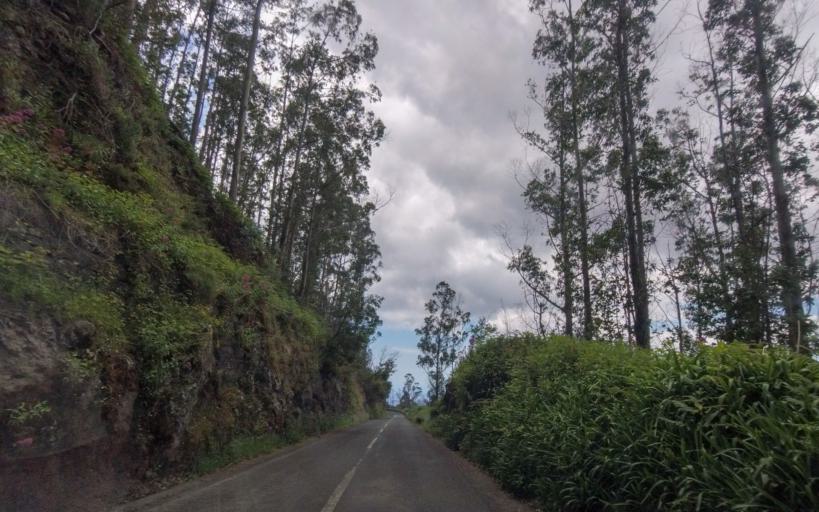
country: PT
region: Madeira
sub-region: Funchal
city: Nossa Senhora do Monte
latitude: 32.6761
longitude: -16.8834
